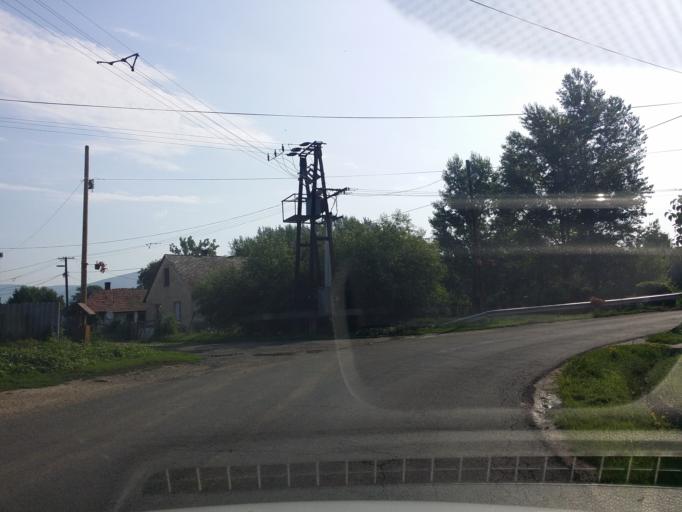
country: HU
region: Borsod-Abauj-Zemplen
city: Gonc
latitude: 48.3781
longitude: 21.2420
